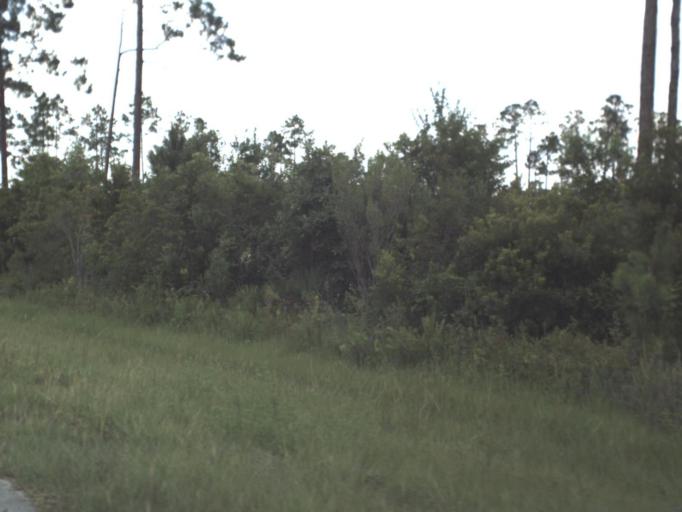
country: US
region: Florida
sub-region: Baker County
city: Macclenny
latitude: 30.5274
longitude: -82.3034
